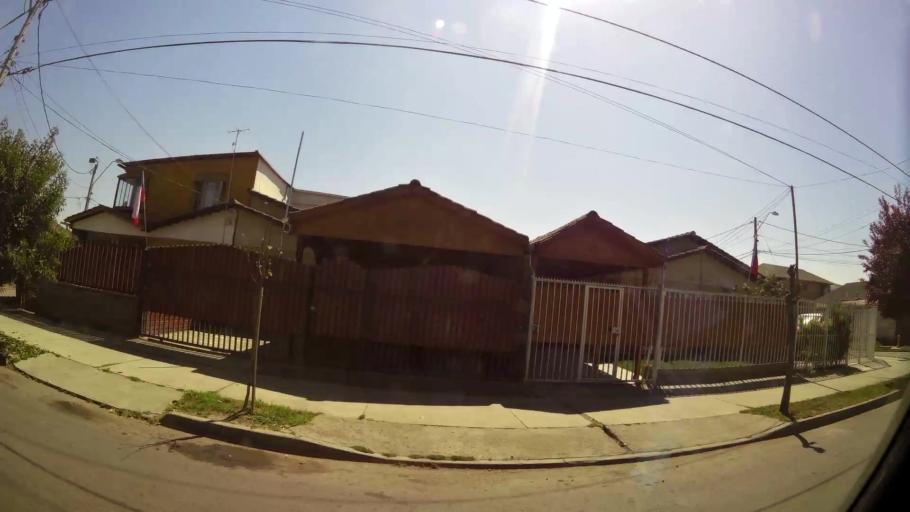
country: CL
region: Santiago Metropolitan
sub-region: Provincia de Talagante
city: Penaflor
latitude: -33.5709
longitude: -70.8125
